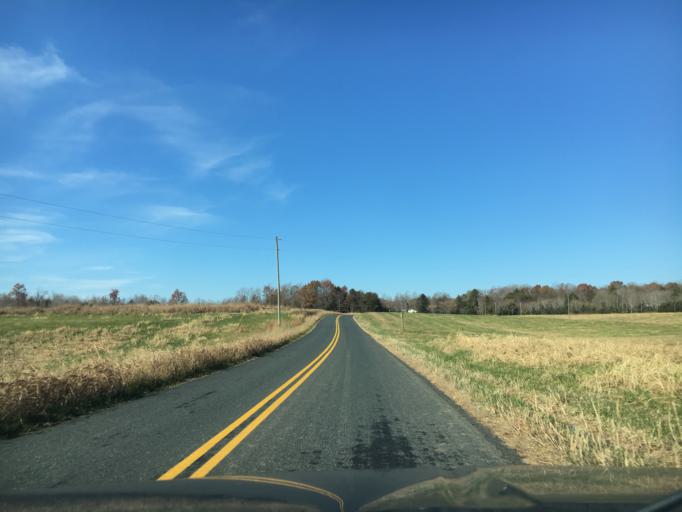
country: US
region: Virginia
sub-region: Buckingham County
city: Buckingham
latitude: 37.4234
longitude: -78.6116
